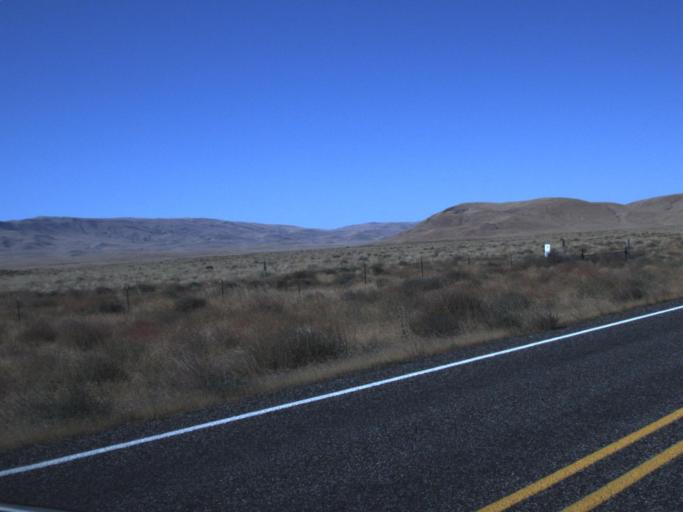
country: US
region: Washington
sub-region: Benton County
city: Benton City
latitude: 46.5108
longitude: -119.6583
